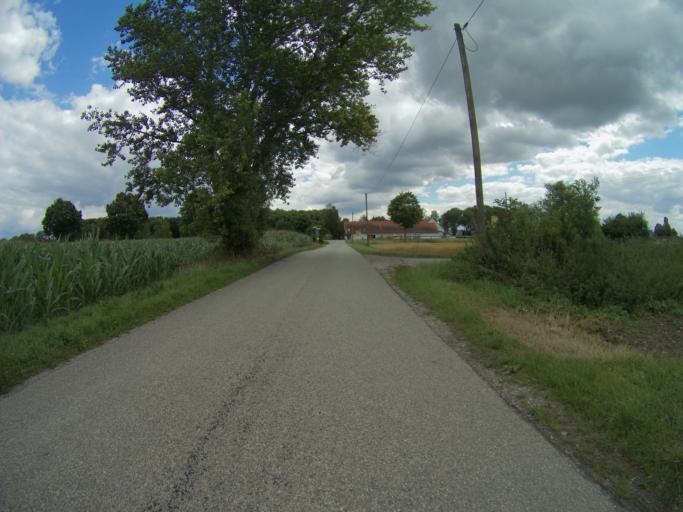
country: DE
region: Bavaria
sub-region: Upper Bavaria
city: Hallbergmoos
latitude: 48.3371
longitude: 11.7291
